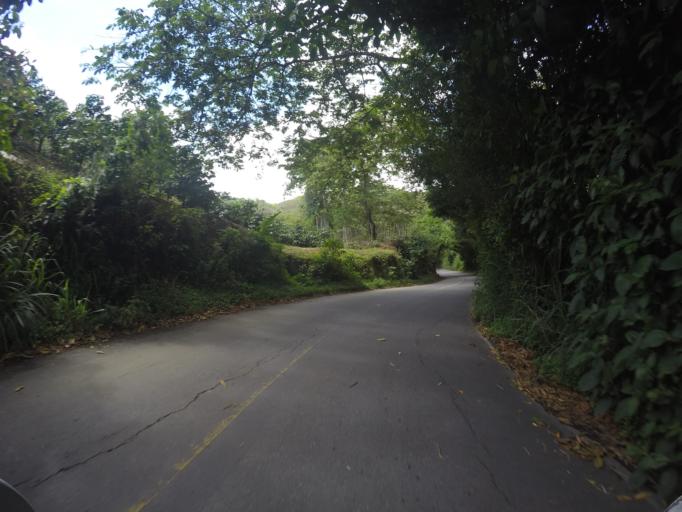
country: CO
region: Quindio
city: Quimbaya
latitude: 4.6268
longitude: -75.7437
